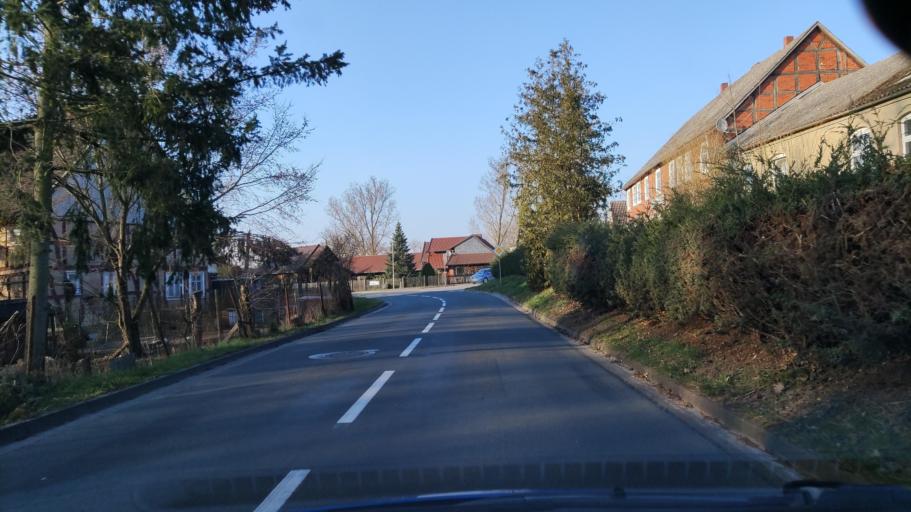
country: DE
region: Brandenburg
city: Cumlosen
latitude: 52.9889
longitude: 11.6080
